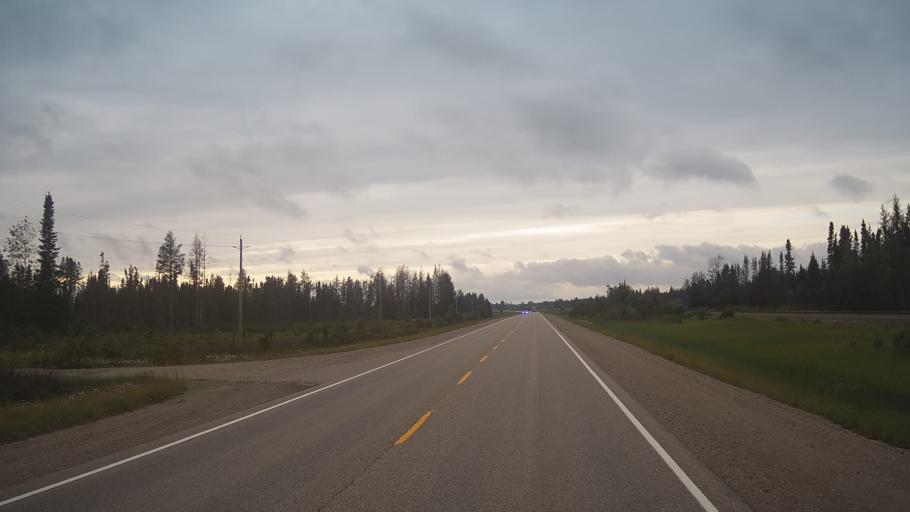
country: CA
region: Ontario
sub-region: Thunder Bay District
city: Thunder Bay
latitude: 48.8689
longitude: -89.9734
